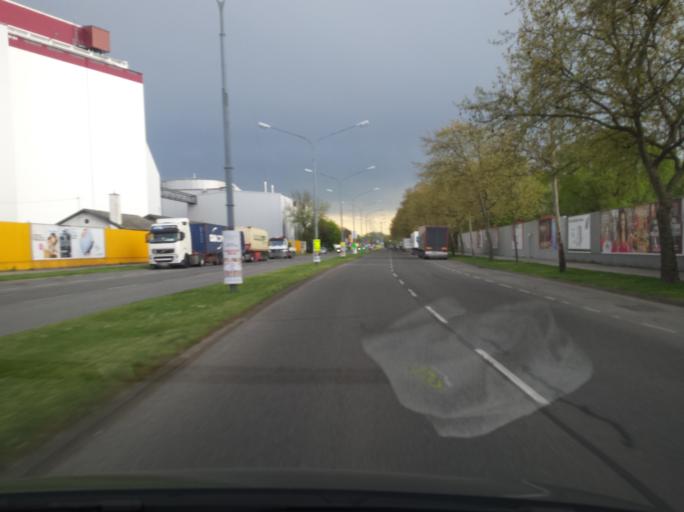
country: AT
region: Lower Austria
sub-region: Politischer Bezirk Wien-Umgebung
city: Gerasdorf bei Wien
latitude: 48.2254
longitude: 16.4447
